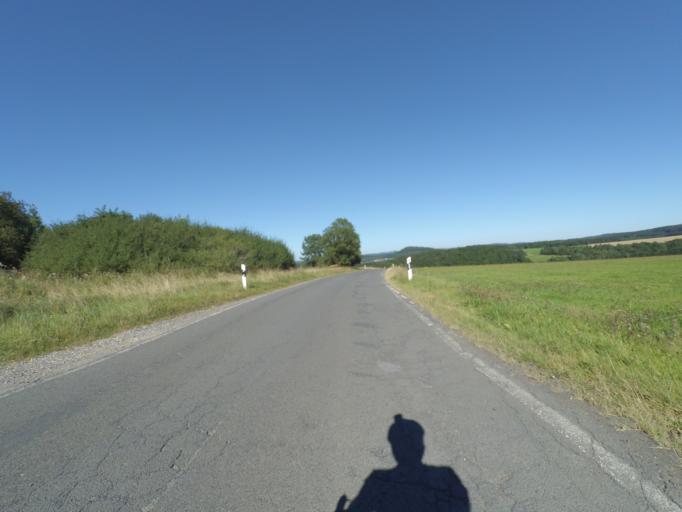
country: DE
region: Rheinland-Pfalz
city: Dreis-Bruck
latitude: 50.2783
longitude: 6.8158
